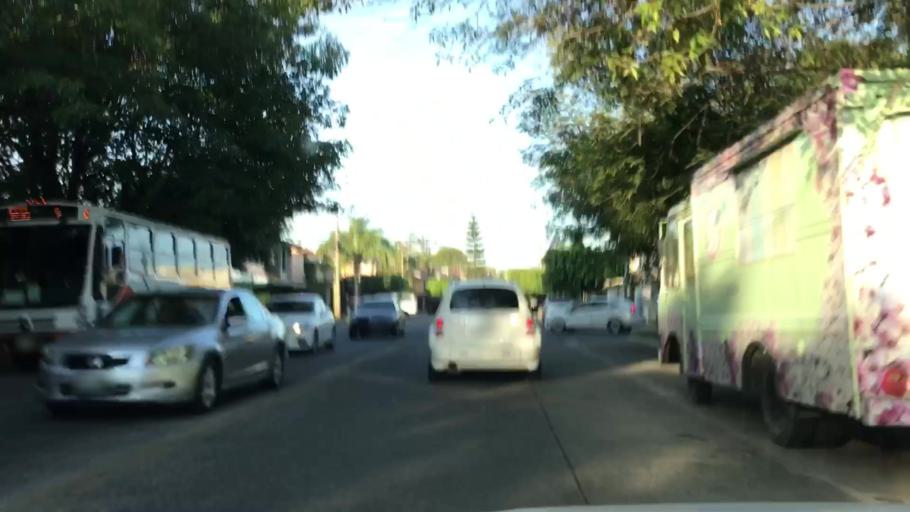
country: MX
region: Jalisco
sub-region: Tlajomulco de Zuniga
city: Palomar
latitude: 20.6340
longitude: -103.4329
